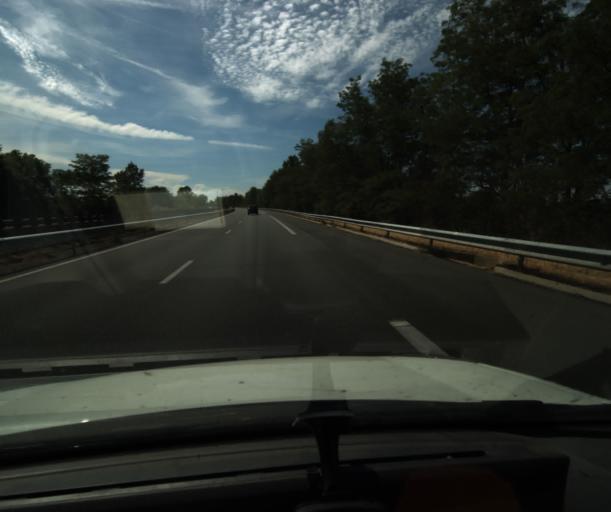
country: FR
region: Midi-Pyrenees
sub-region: Departement du Tarn-et-Garonne
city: Castelsarrasin
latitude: 44.0565
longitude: 1.1182
